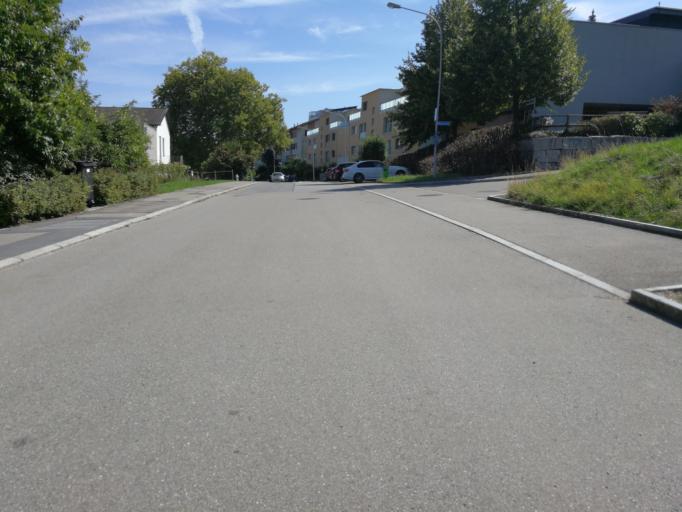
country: CH
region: Zurich
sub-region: Bezirk Horgen
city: Au / Mittel-Dorf
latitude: 47.2454
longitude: 8.6445
